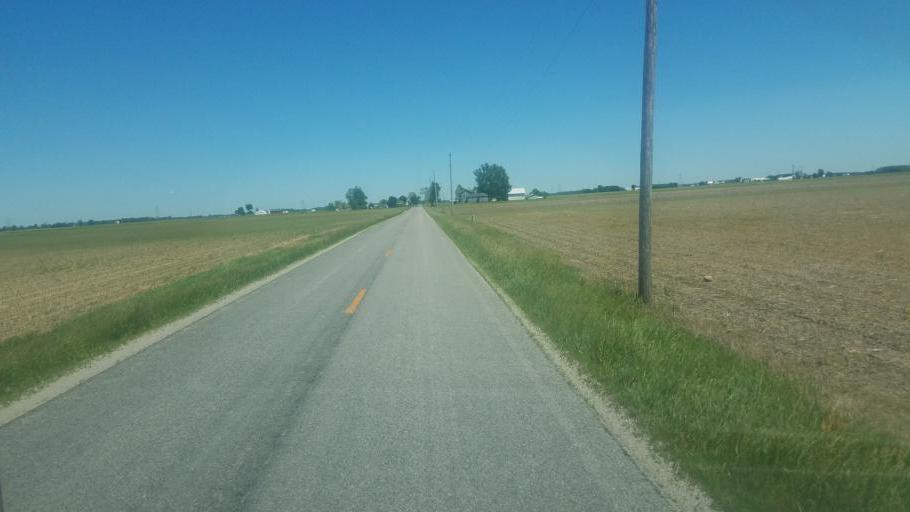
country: US
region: Ohio
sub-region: Shelby County
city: Sidney
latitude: 40.2108
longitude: -84.1118
